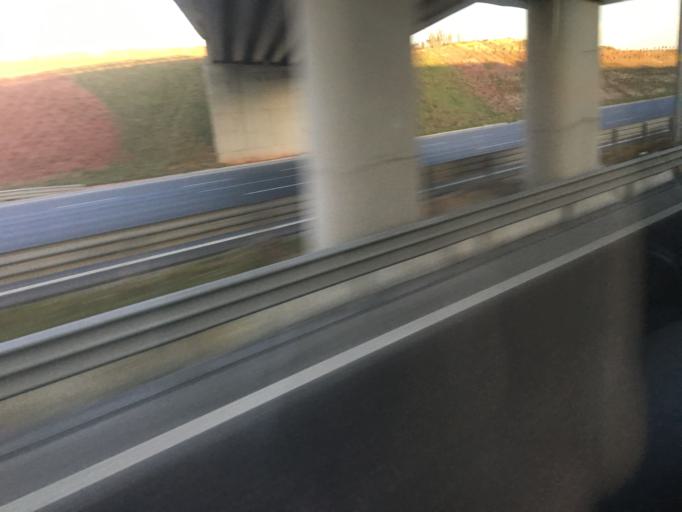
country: TR
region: Istanbul
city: Mahmut Sevket Pasa
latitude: 41.1196
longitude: 29.2877
